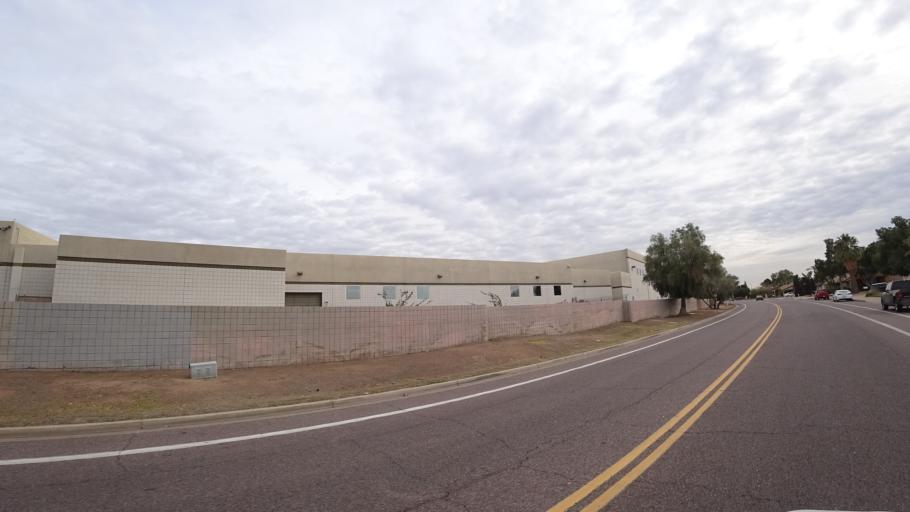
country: US
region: Arizona
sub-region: Maricopa County
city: Glendale
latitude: 33.6295
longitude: -112.1212
